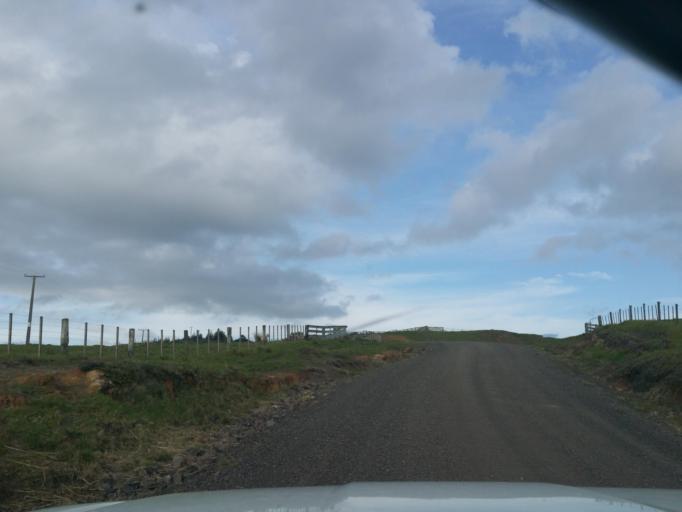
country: NZ
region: Northland
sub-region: Kaipara District
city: Dargaville
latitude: -35.8654
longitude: 173.7301
